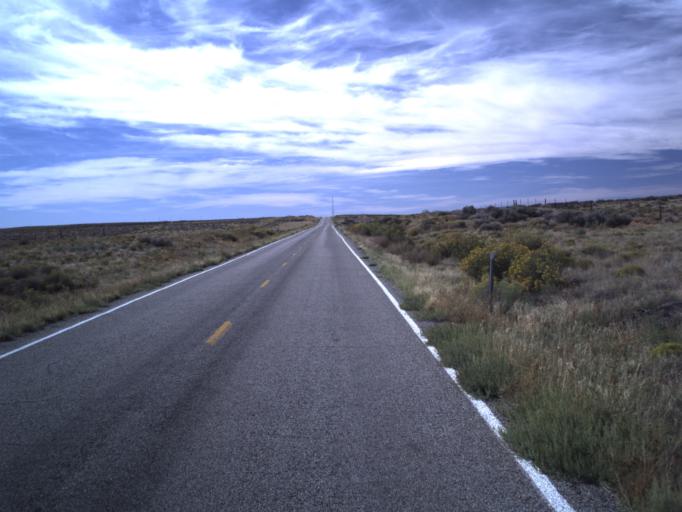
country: US
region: Utah
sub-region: San Juan County
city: Blanding
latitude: 37.3476
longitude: -109.3479
